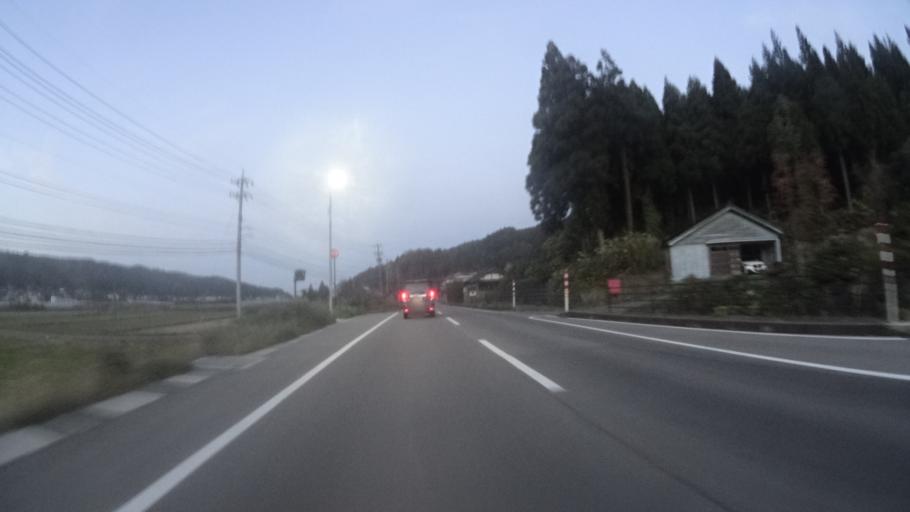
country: JP
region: Ishikawa
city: Nanao
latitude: 37.3690
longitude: 136.8737
